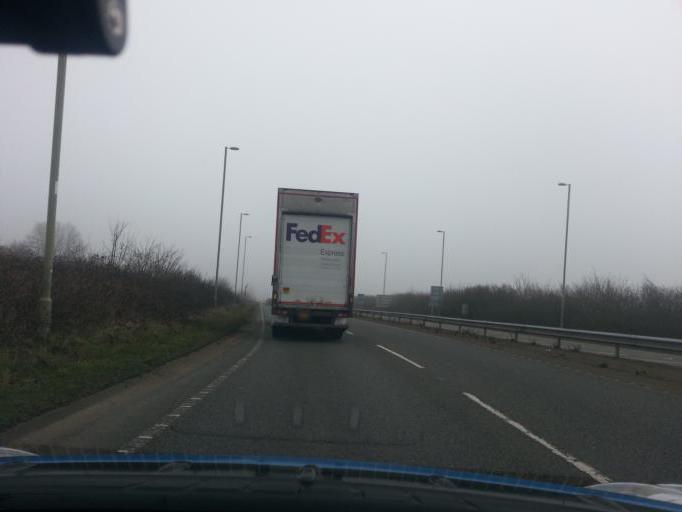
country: GB
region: England
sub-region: Oxfordshire
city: Frilford
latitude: 51.6854
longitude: -1.4115
